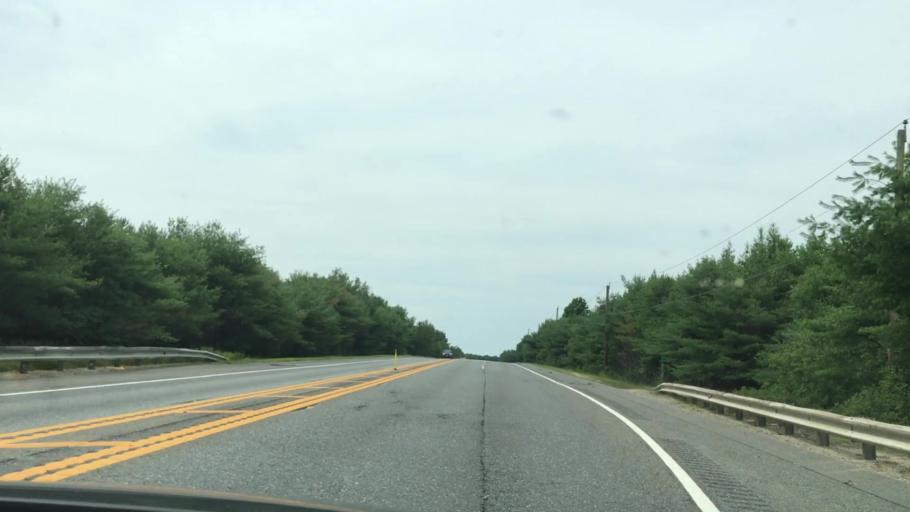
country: US
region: Massachusetts
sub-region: Worcester County
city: Gardner
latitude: 42.6103
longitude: -71.9980
